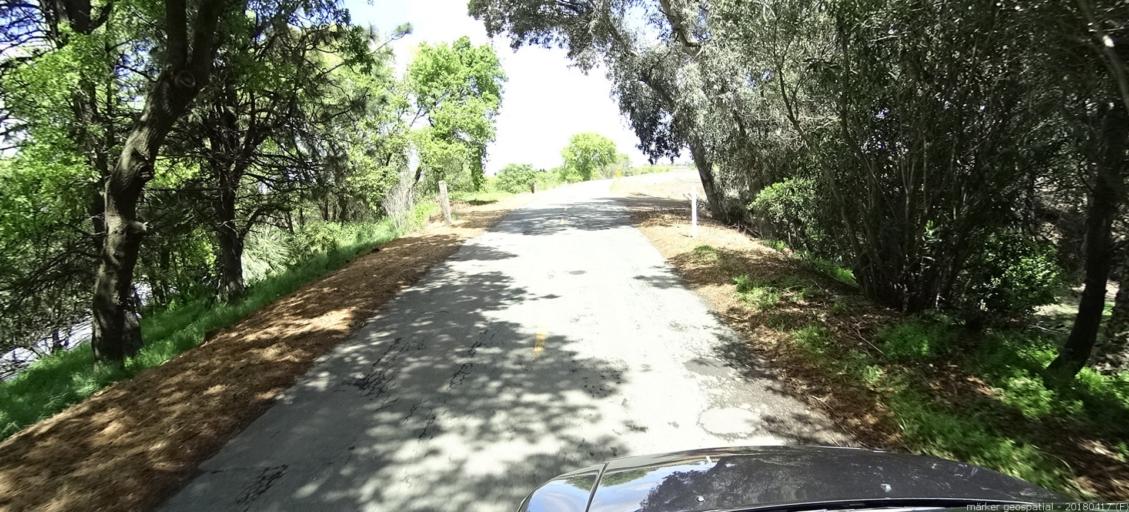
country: US
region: California
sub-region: Sacramento County
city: Walnut Grove
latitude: 38.1790
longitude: -121.5785
